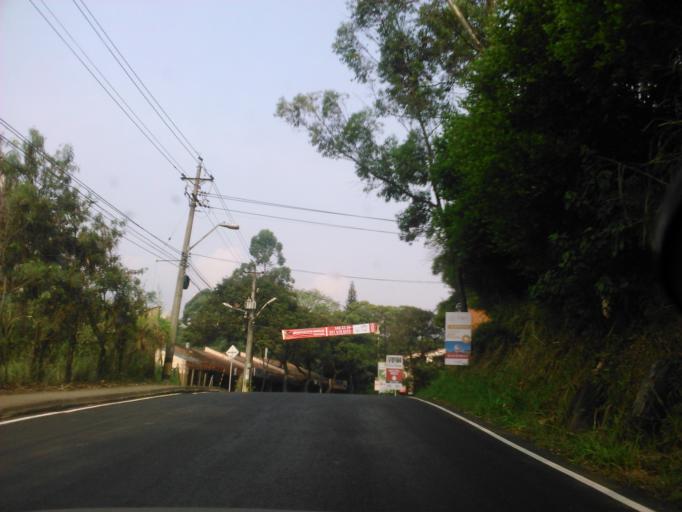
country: CO
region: Antioquia
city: Sabaneta
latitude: 6.1577
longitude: -75.6226
